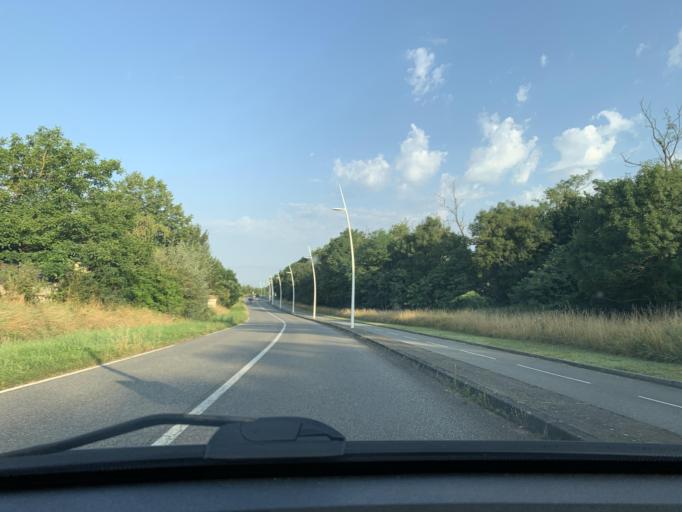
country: FR
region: Midi-Pyrenees
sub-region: Departement de la Haute-Garonne
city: Labege
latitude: 43.5340
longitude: 1.5452
